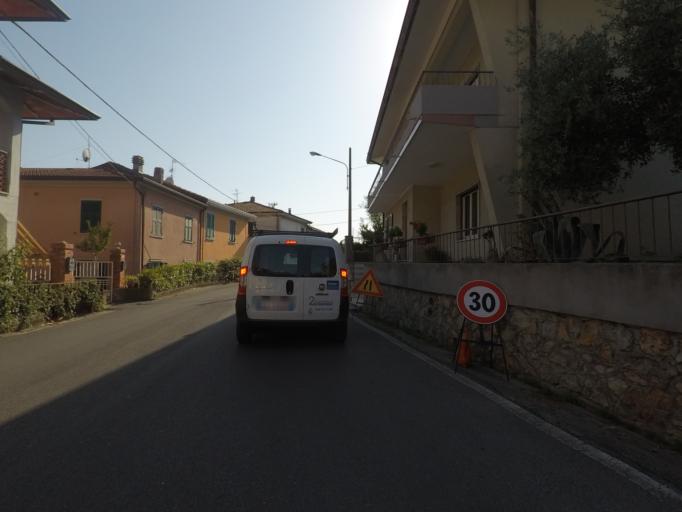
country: IT
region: Liguria
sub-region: Provincia di La Spezia
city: Casano-Dogana-Isola
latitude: 44.0839
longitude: 10.0398
